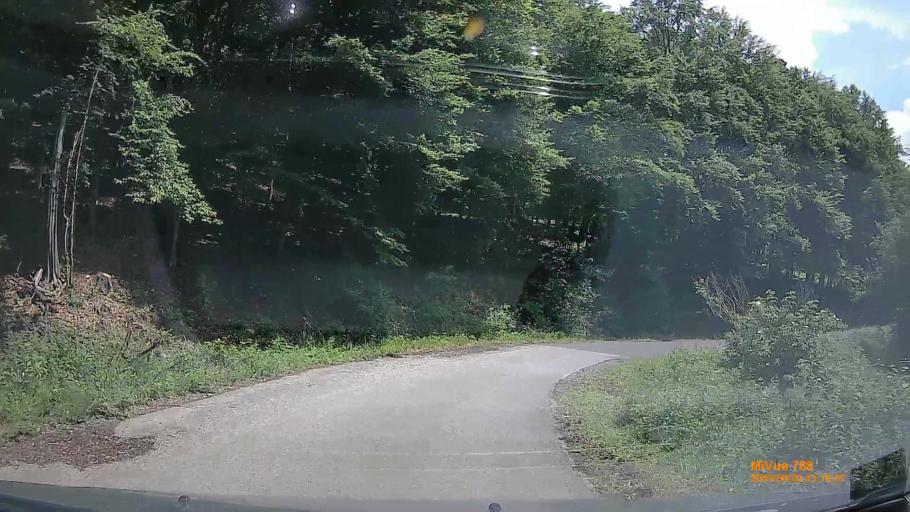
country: HU
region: Baranya
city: Hosszuheteny
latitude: 46.1916
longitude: 18.3450
